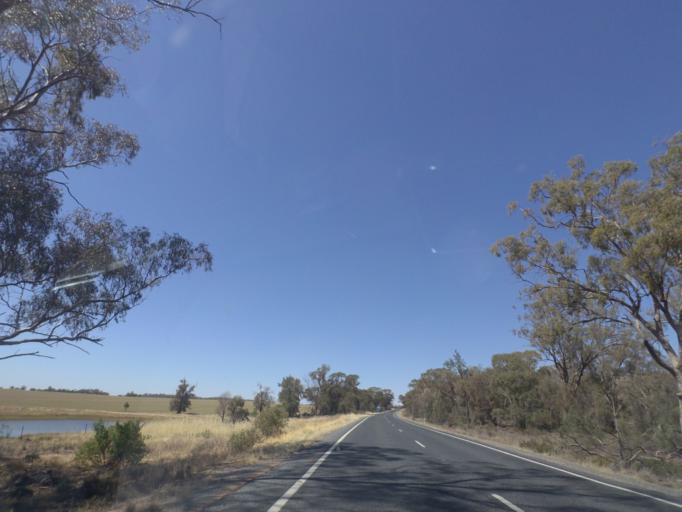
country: AU
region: New South Wales
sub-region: Narrandera
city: Narrandera
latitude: -34.4402
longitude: 146.8414
